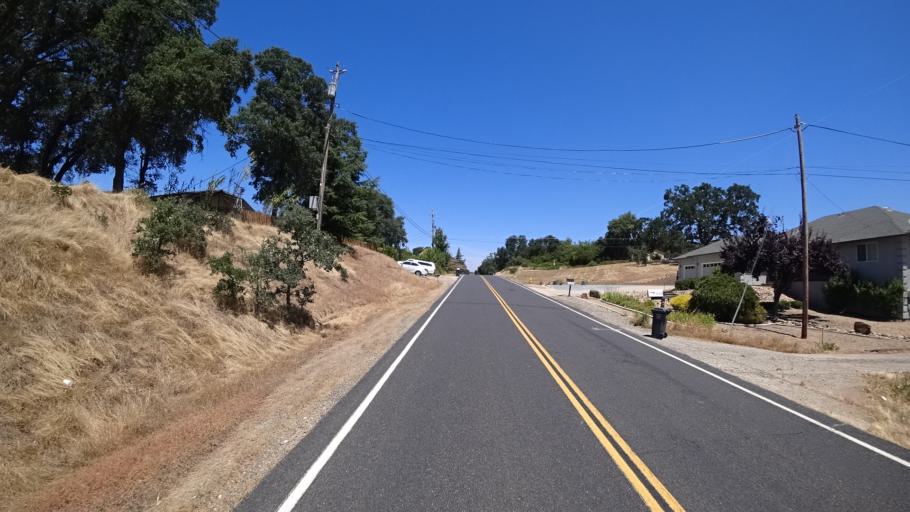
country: US
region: California
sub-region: Calaveras County
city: Rancho Calaveras
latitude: 38.1260
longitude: -120.8670
